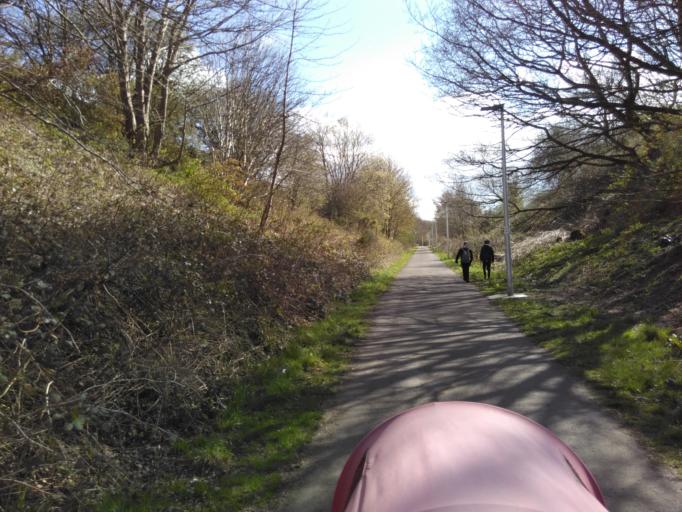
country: GB
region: Scotland
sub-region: Midlothian
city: Loanhead
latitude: 55.8747
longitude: -3.1502
